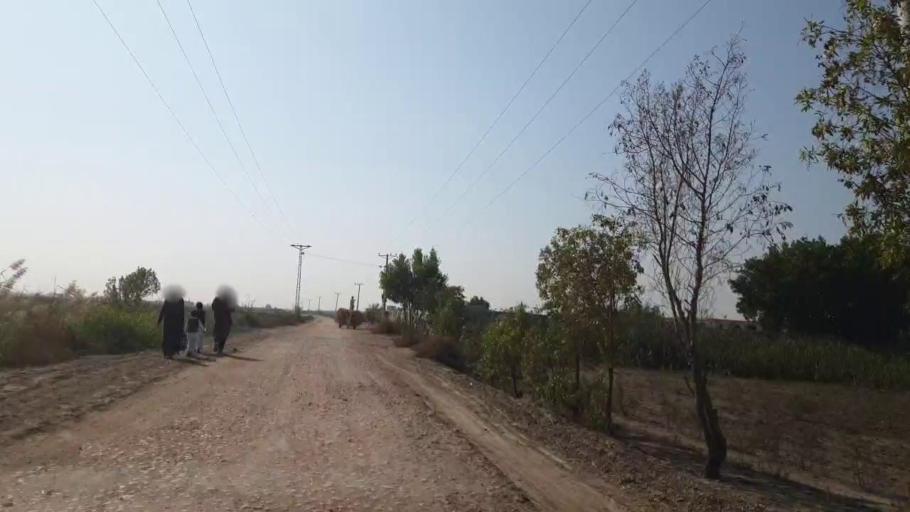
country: PK
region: Sindh
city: Thatta
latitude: 24.7386
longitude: 67.7945
